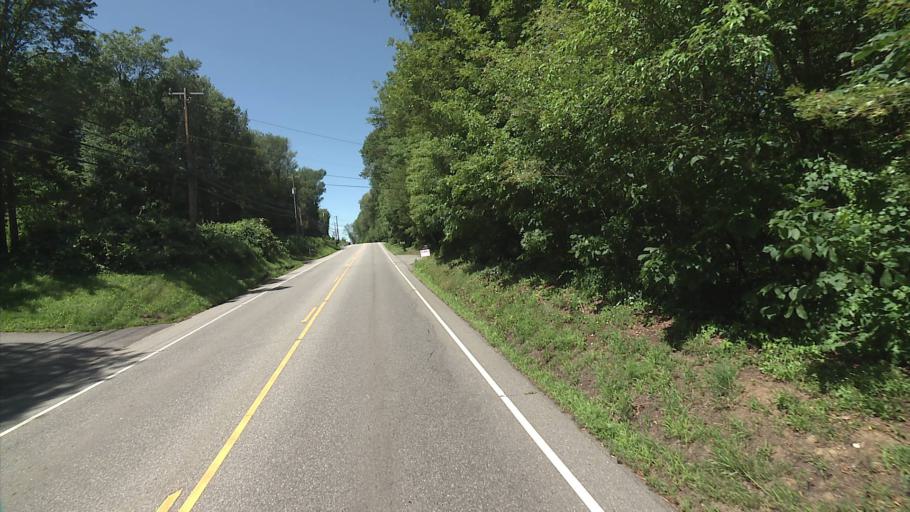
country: US
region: Connecticut
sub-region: New London County
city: Colchester
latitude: 41.5636
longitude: -72.3550
